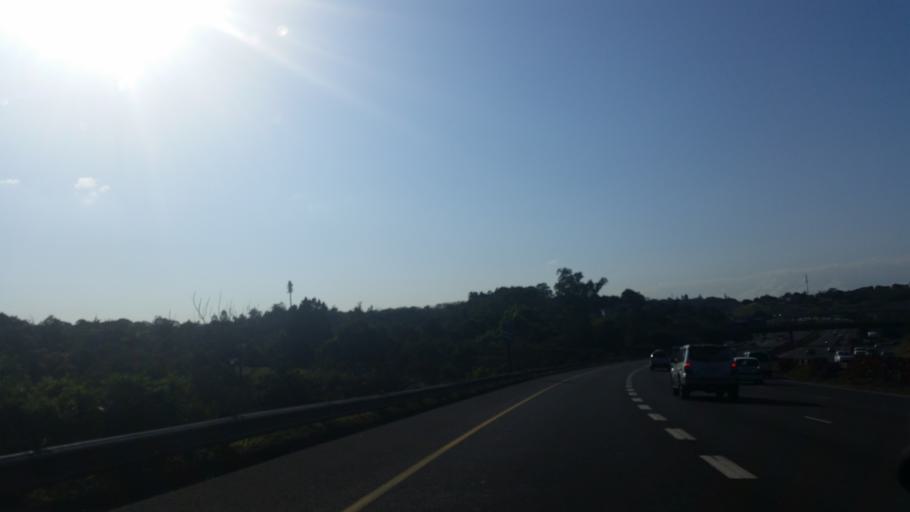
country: ZA
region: KwaZulu-Natal
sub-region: eThekwini Metropolitan Municipality
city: Berea
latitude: -29.8403
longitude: 30.9488
